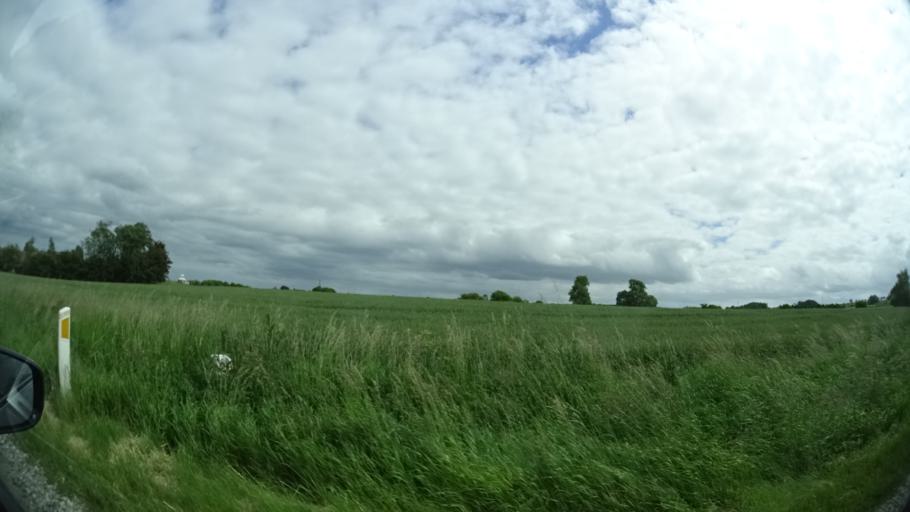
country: DK
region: Central Jutland
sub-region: Syddjurs Kommune
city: Ronde
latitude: 56.3447
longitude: 10.4528
